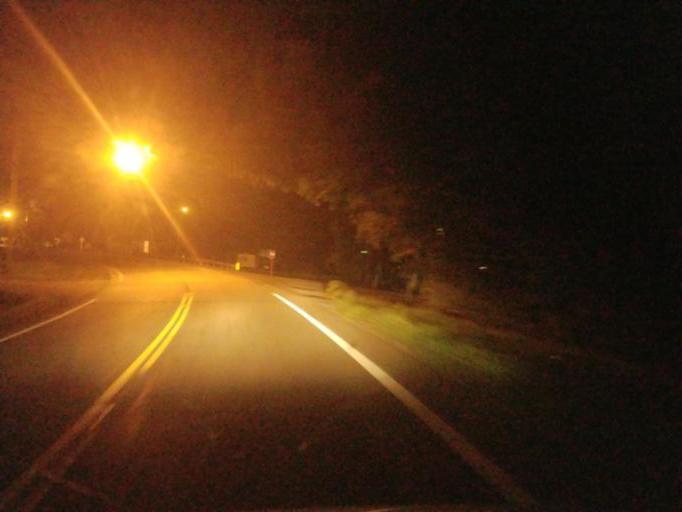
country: US
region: Ohio
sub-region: Stark County
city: Minerva
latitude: 40.7475
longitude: -81.0690
